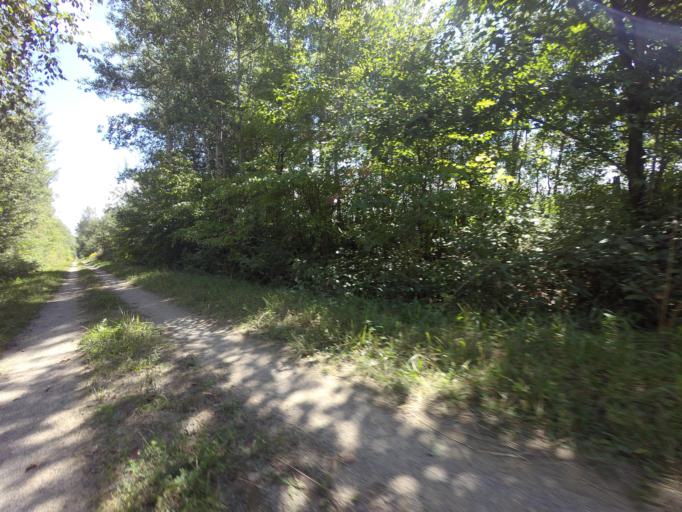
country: CA
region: Ontario
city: Orangeville
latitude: 43.7788
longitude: -80.2106
